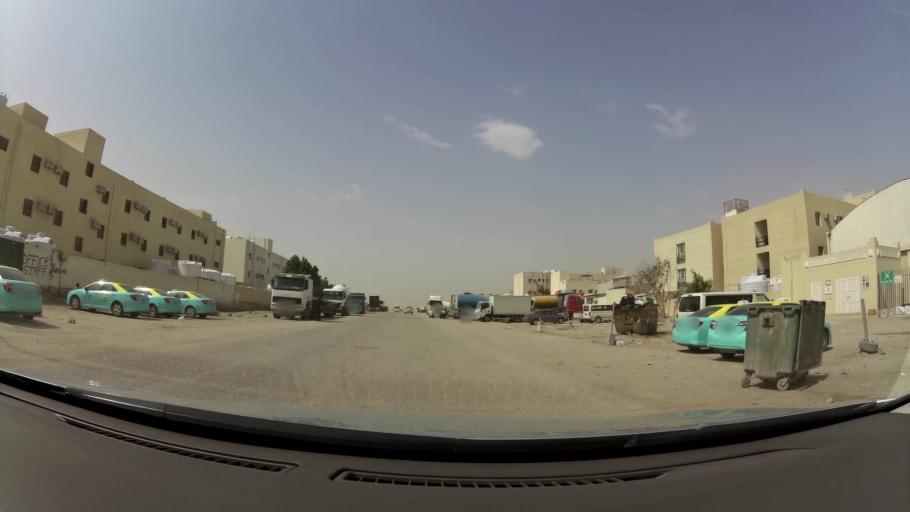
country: QA
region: Al Wakrah
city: Al Wukayr
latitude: 25.1665
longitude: 51.4586
